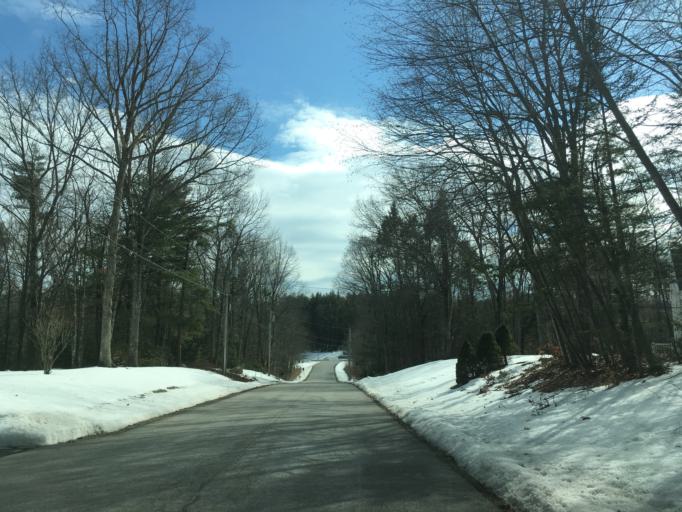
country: US
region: New Hampshire
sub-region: Rockingham County
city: Exeter
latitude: 42.9857
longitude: -70.8898
